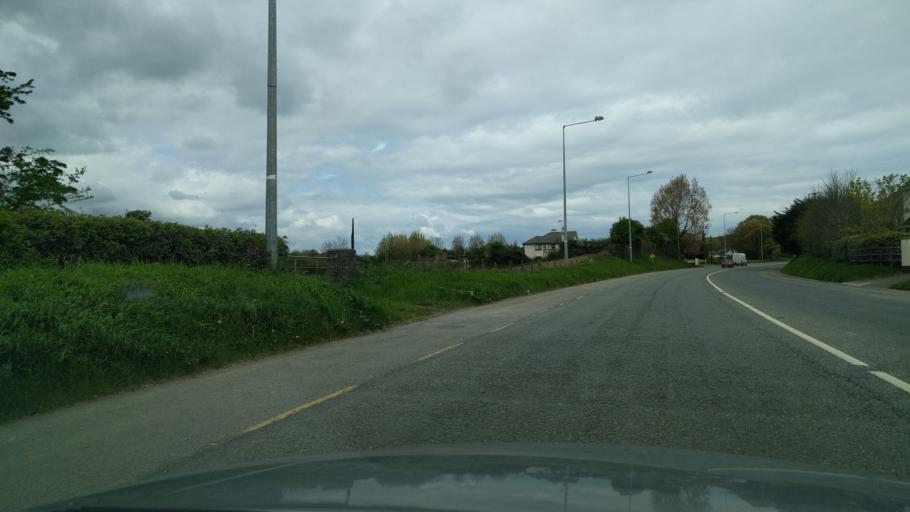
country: IE
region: Leinster
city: Balrothery
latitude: 53.5903
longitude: -6.1884
